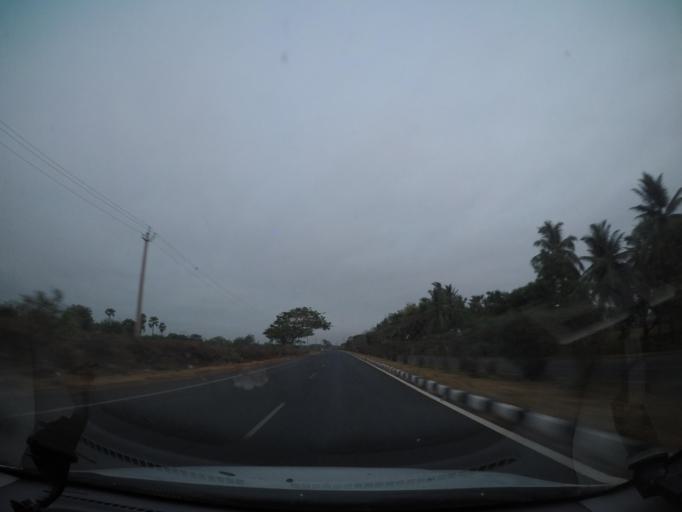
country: IN
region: Andhra Pradesh
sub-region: West Godavari
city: Tadepallegudem
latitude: 16.8071
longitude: 81.3126
